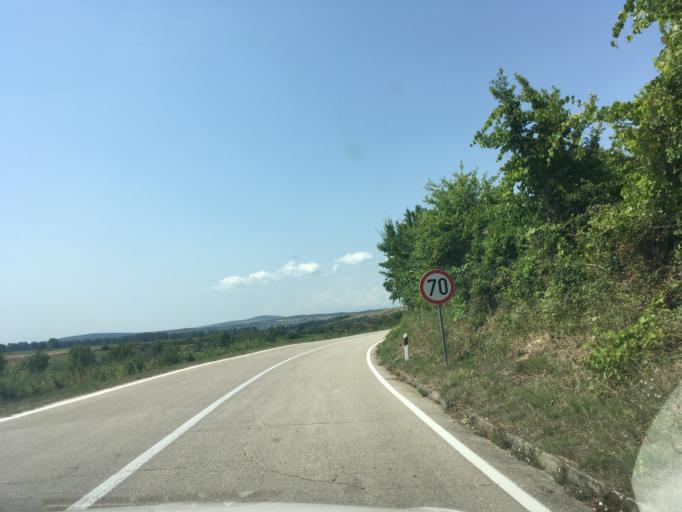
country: HR
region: Sibensko-Kniniska
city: Zaton
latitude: 43.9319
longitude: 15.7959
